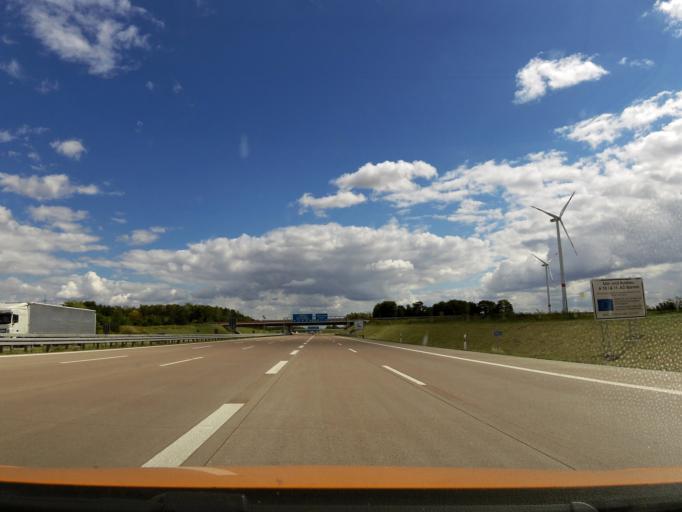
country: DE
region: Berlin
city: Buch
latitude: 52.6156
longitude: 13.5339
